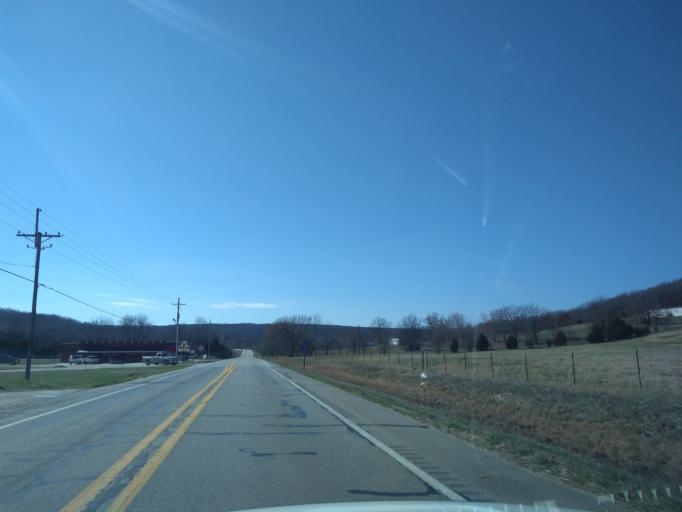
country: US
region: Arkansas
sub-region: Washington County
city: Prairie Grove
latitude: 35.9600
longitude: -94.3566
